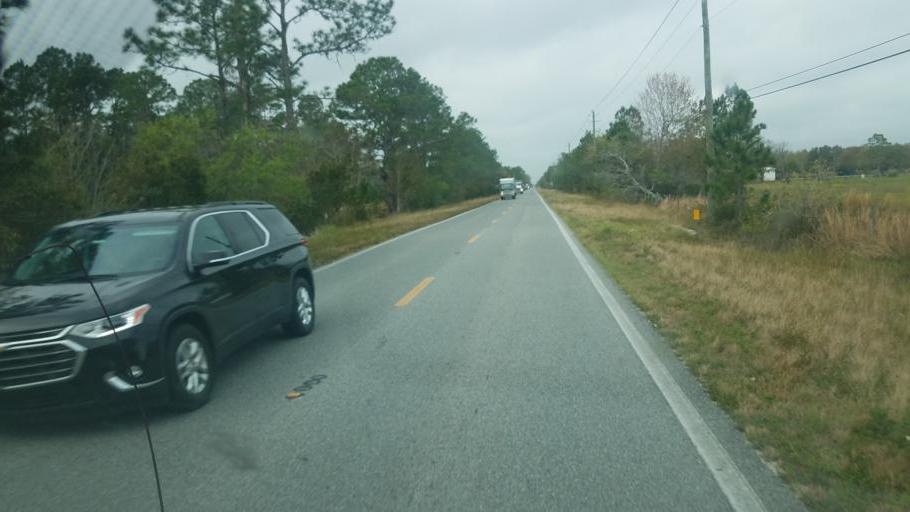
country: US
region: Florida
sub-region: Polk County
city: Polk City
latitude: 28.2590
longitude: -81.8923
